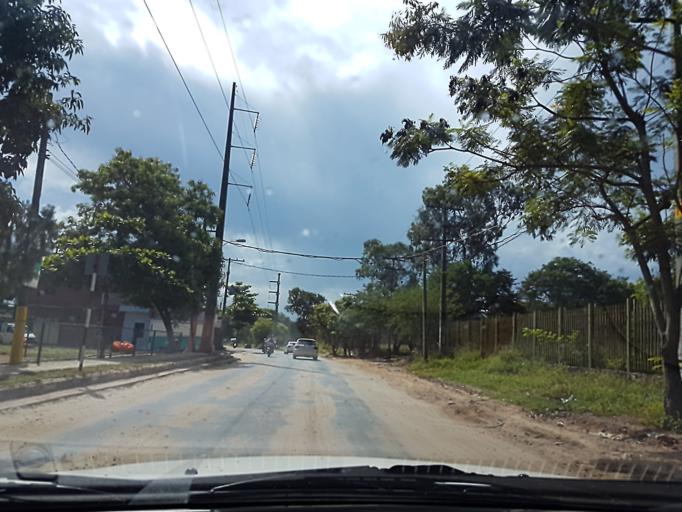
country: PY
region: Asuncion
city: Asuncion
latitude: -25.2434
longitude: -57.5800
